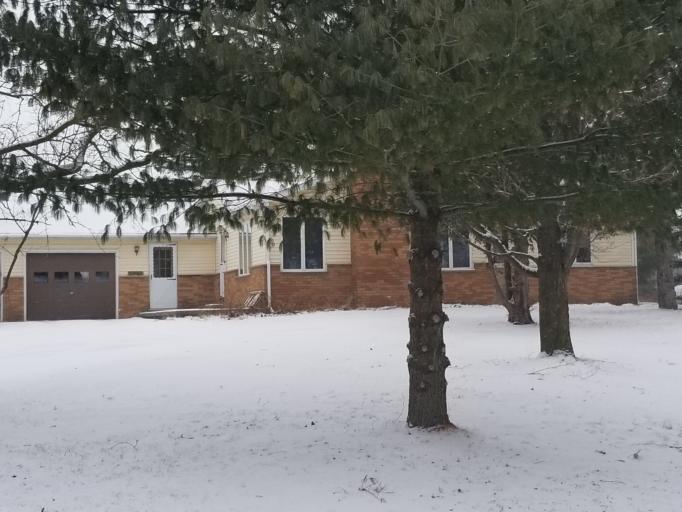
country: US
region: Michigan
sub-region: Osceola County
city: Evart
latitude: 44.1039
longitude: -85.2062
